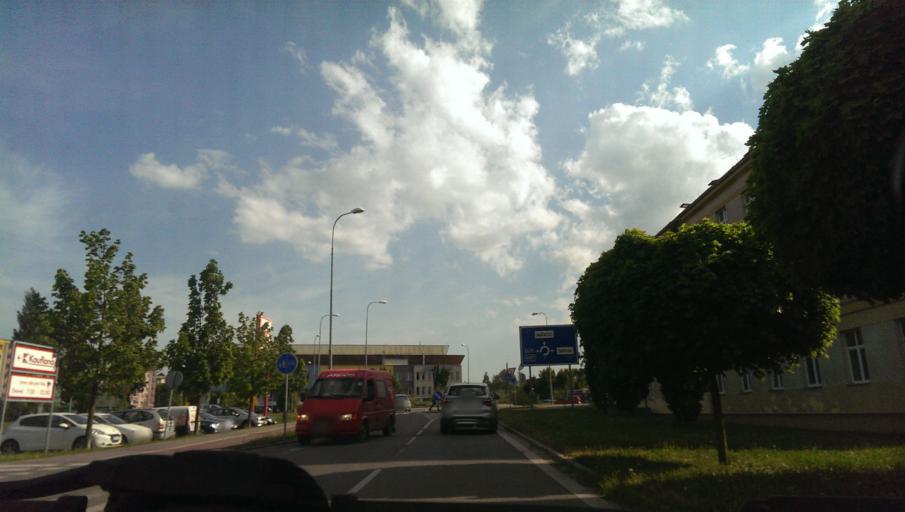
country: CZ
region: Zlin
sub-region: Okres Uherske Hradiste
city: Uherske Hradiste
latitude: 49.0701
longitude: 17.4732
